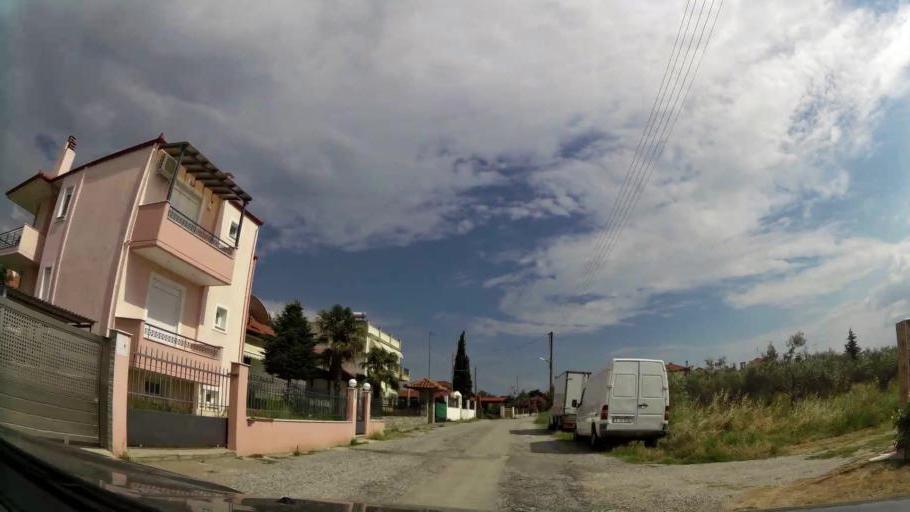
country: GR
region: Central Macedonia
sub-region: Nomos Pierias
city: Makrygialos
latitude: 40.4198
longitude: 22.6070
